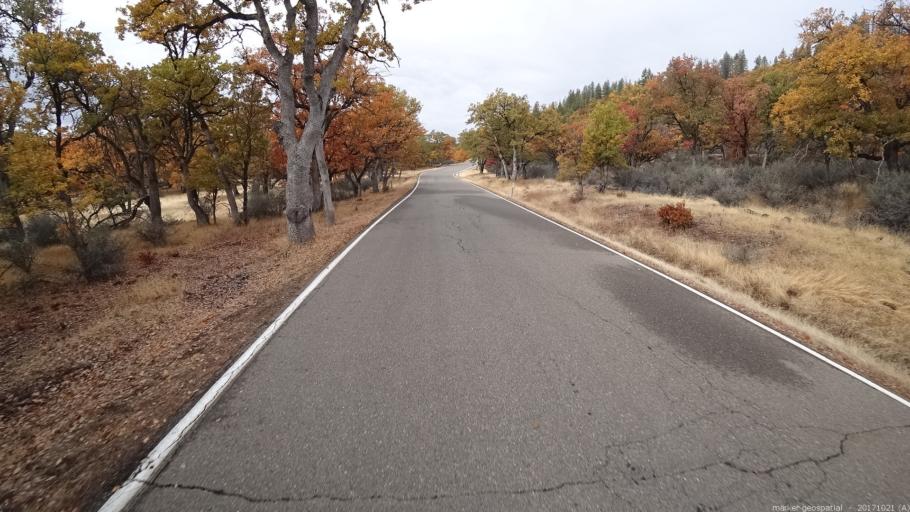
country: US
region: California
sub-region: Shasta County
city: Burney
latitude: 41.0418
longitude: -121.6553
